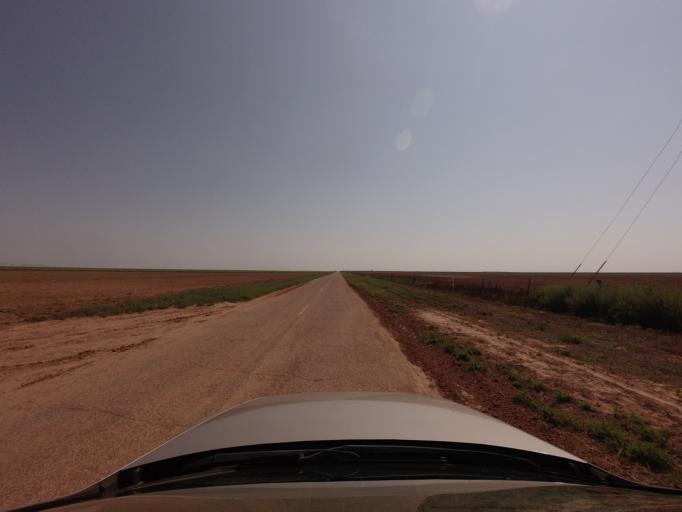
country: US
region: New Mexico
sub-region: Curry County
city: Cannon Air Force Base
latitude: 34.6330
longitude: -103.3639
